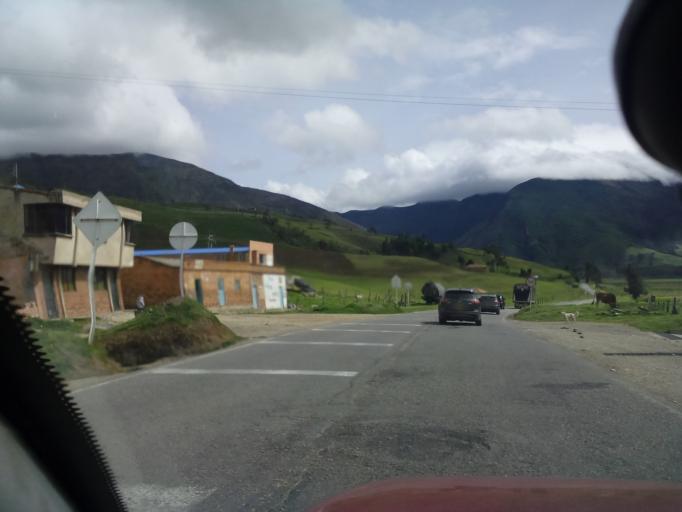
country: CO
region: Boyaca
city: Combita
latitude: 5.6922
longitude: -73.3679
